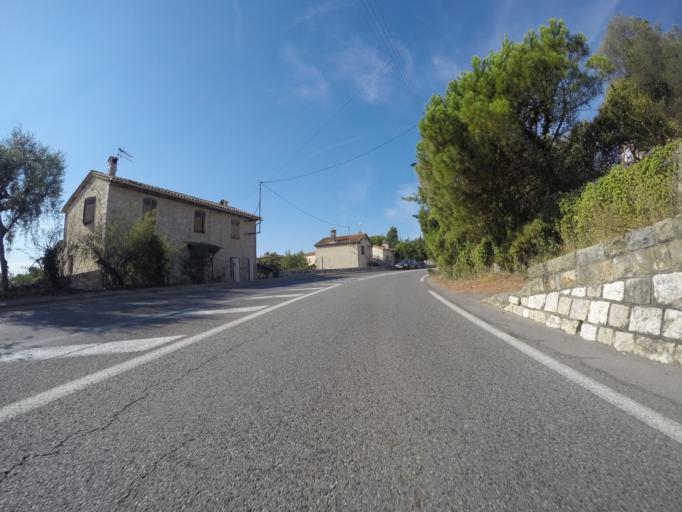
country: FR
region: Provence-Alpes-Cote d'Azur
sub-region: Departement des Alpes-Maritimes
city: La Colle-sur-Loup
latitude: 43.6645
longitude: 7.0641
